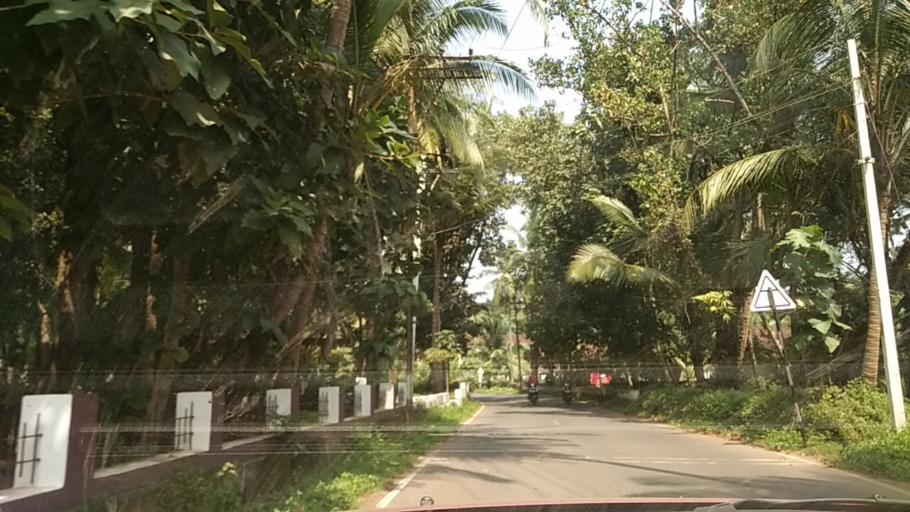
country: IN
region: Goa
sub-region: South Goa
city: Sancoale
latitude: 15.3399
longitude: 73.8999
